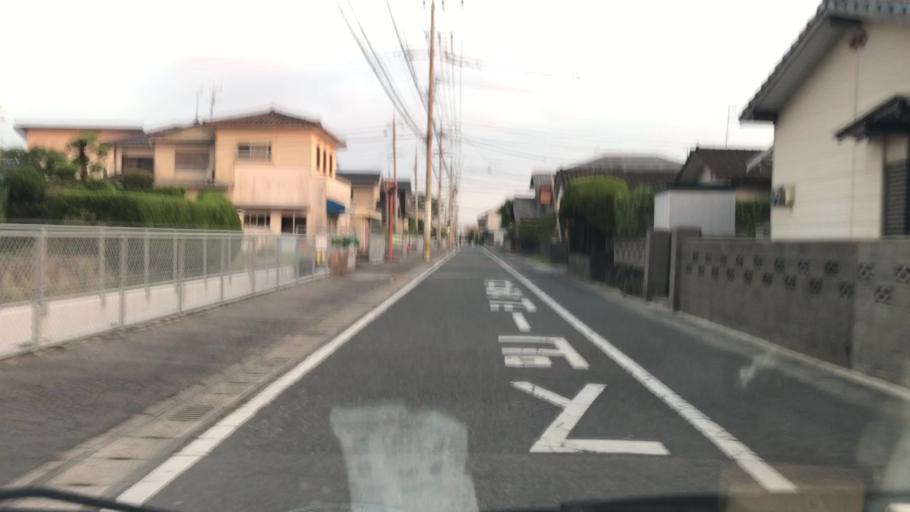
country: JP
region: Saga Prefecture
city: Saga-shi
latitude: 33.2461
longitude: 130.2574
